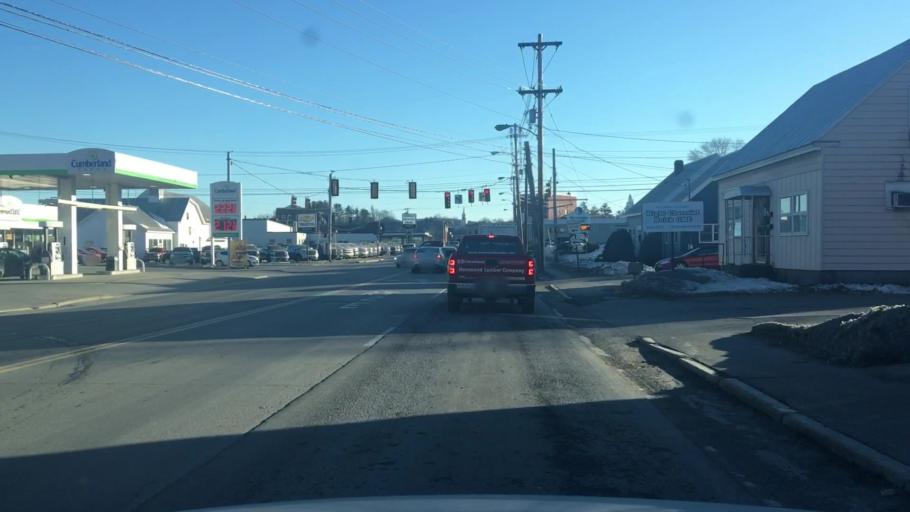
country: US
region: Maine
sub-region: Somerset County
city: Skowhegan
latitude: 44.7677
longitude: -69.7206
